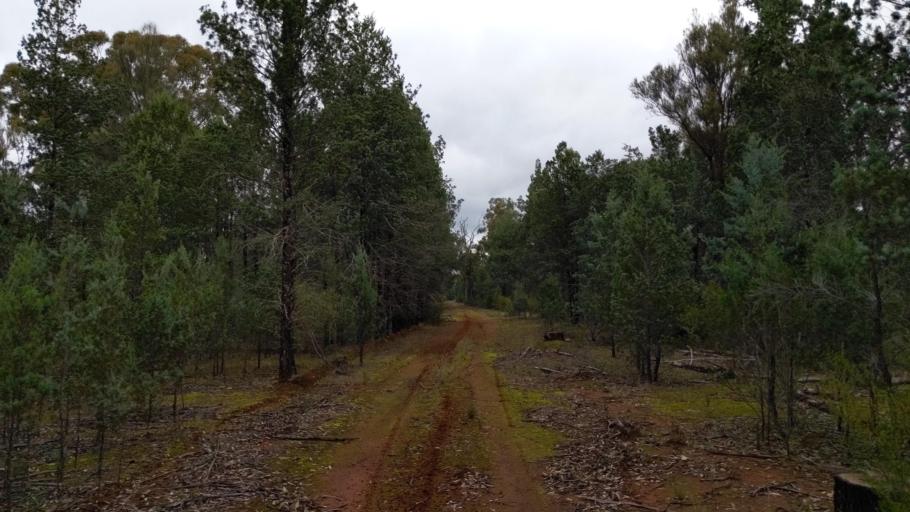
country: AU
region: New South Wales
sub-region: Coolamon
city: Coolamon
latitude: -34.8440
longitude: 146.9331
